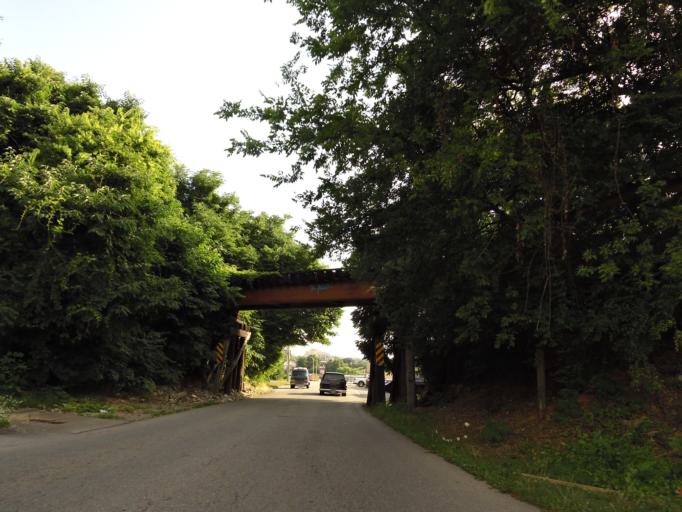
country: US
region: Tennessee
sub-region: Blount County
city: Maryville
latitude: 35.7634
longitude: -83.9636
